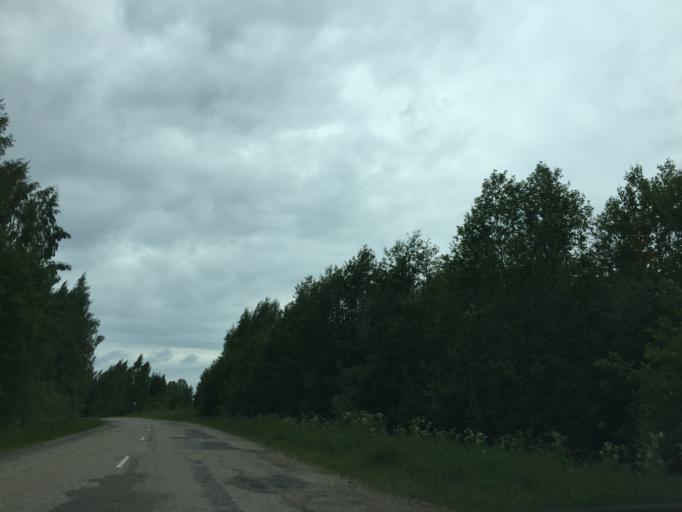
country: LV
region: Varkava
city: Vecvarkava
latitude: 56.0897
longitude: 26.5727
